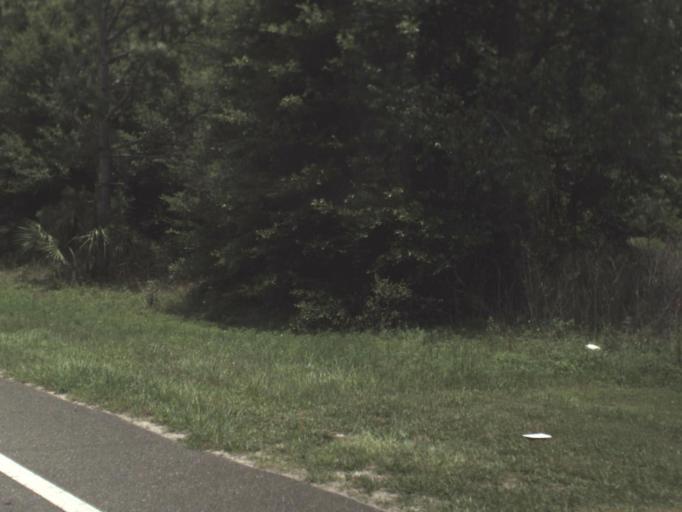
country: US
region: Florida
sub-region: Levy County
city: East Bronson
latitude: 29.4673
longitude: -82.6172
